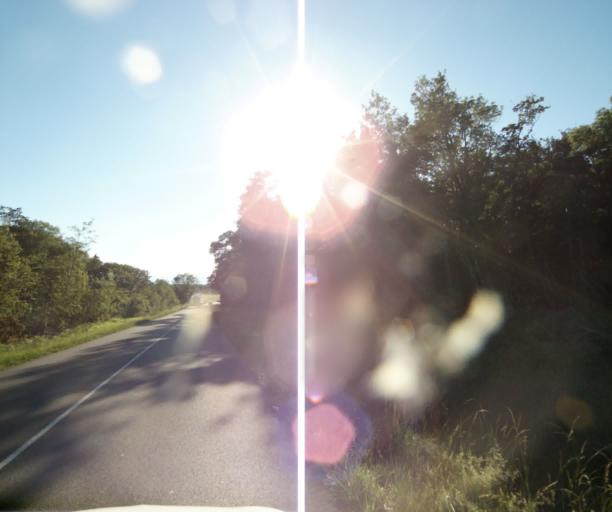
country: FR
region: Rhone-Alpes
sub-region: Departement de la Haute-Savoie
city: Loisin
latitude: 46.2670
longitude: 6.3001
